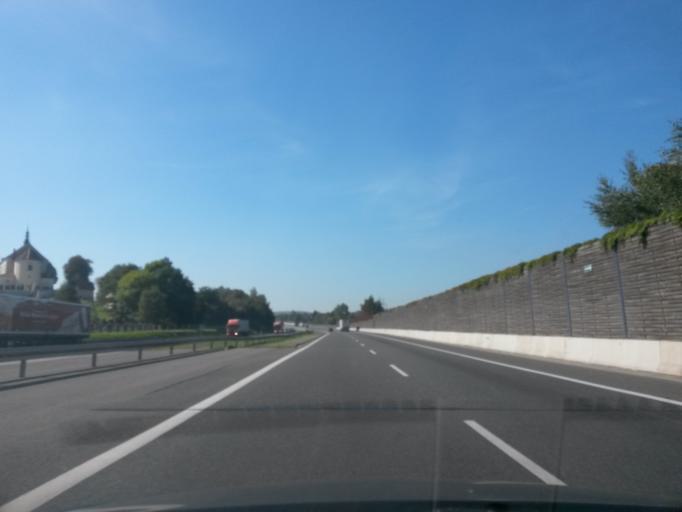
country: PL
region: Lesser Poland Voivodeship
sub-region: Powiat krakowski
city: Mnikow
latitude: 50.0798
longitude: 19.7555
